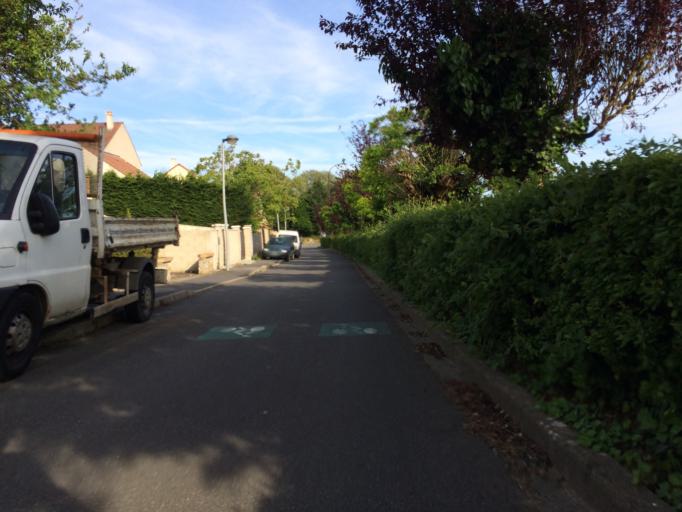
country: FR
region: Ile-de-France
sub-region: Departement de l'Essonne
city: Montlhery
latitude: 48.6448
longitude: 2.2804
